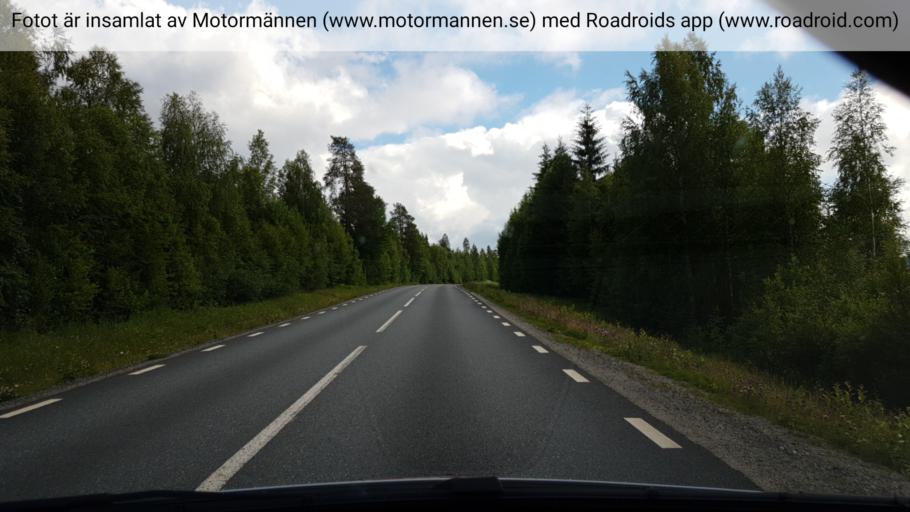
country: SE
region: Vaesterbotten
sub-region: Bjurholms Kommun
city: Bjurholm
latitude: 64.3325
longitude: 19.1505
